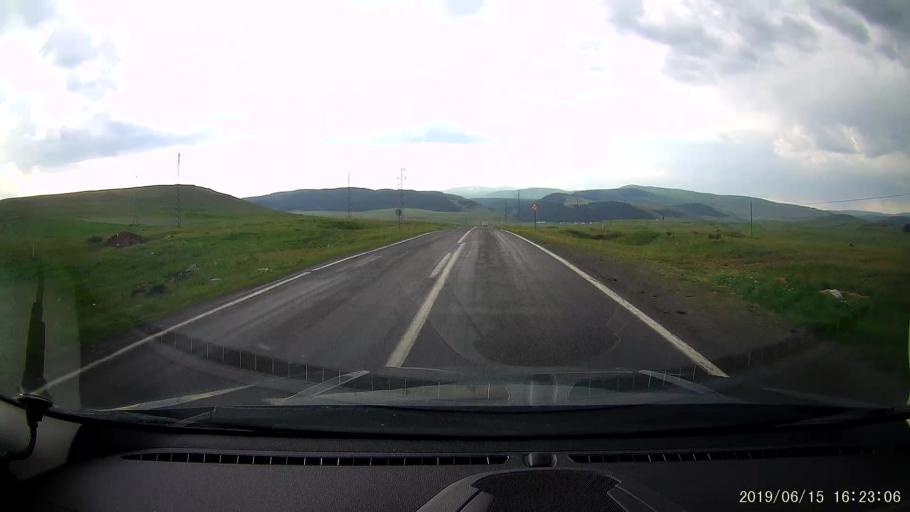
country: TR
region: Ardahan
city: Hanak
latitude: 41.1808
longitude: 42.8582
